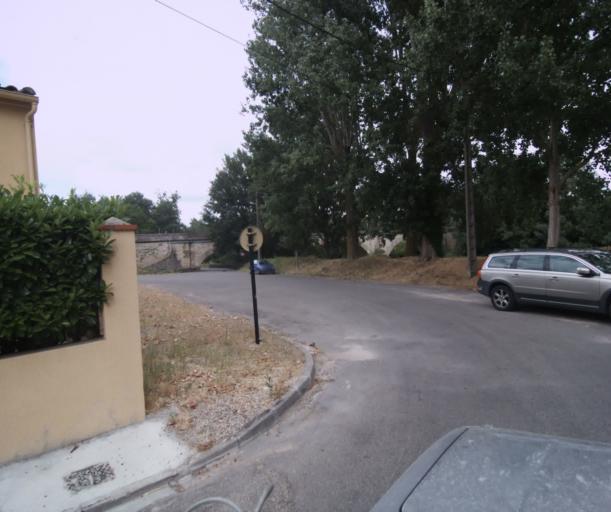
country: FR
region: Languedoc-Roussillon
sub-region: Departement de l'Aude
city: Limoux
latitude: 43.0640
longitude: 2.2187
